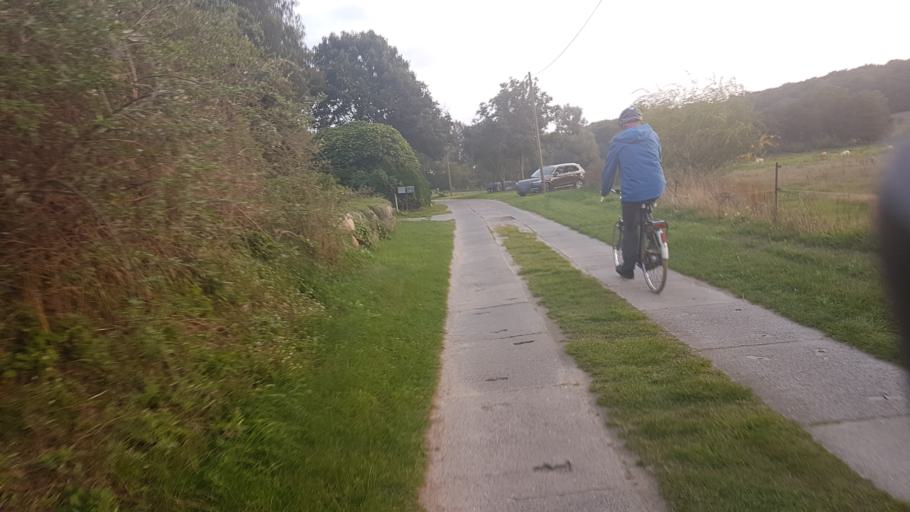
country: DE
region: Mecklenburg-Vorpommern
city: Putbus
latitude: 54.3481
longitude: 13.5360
